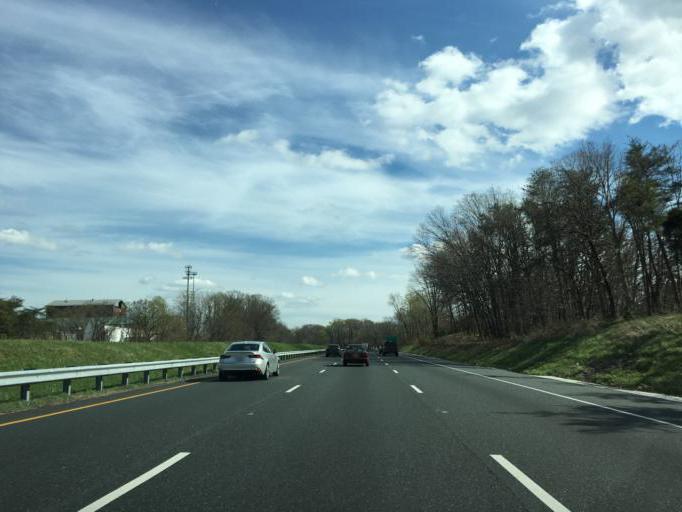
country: US
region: Maryland
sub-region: Baltimore County
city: Mays Chapel
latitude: 39.3830
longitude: -76.6619
